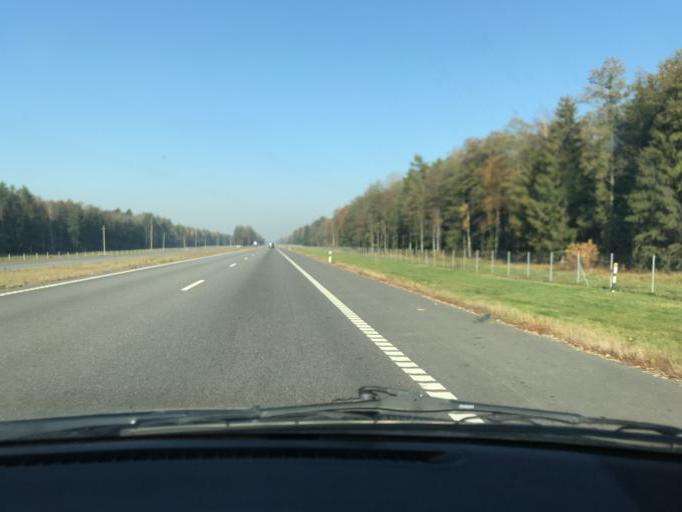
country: BY
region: Minsk
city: Slutsk
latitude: 53.2954
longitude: 27.5460
